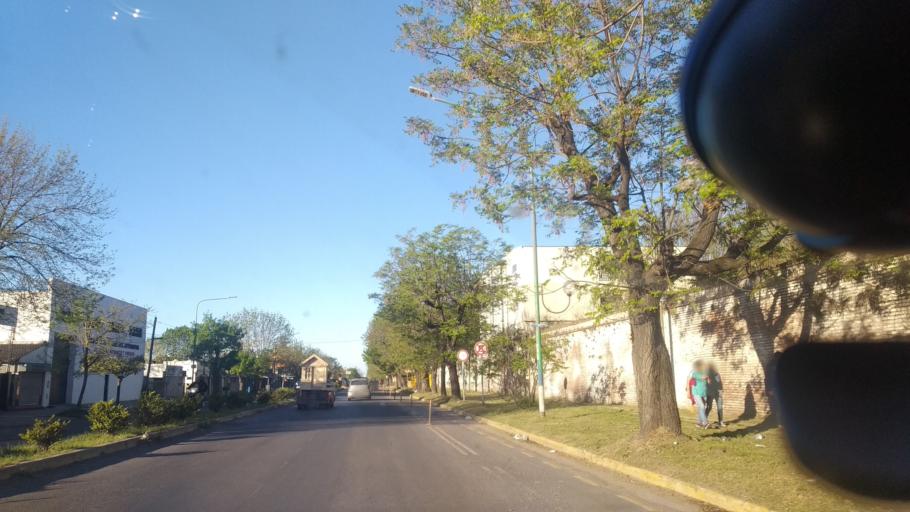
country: AR
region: Buenos Aires
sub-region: Partido de La Plata
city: La Plata
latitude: -34.9568
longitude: -57.9561
